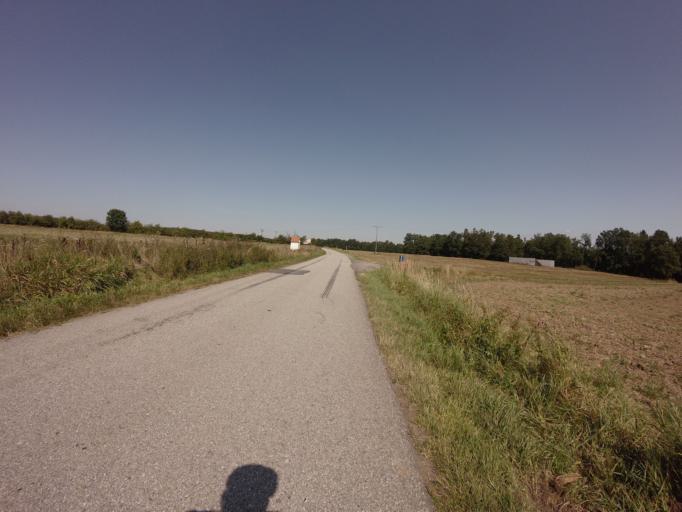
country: CZ
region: Jihocesky
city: Kamenny Ujezd
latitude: 48.9105
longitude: 14.4334
